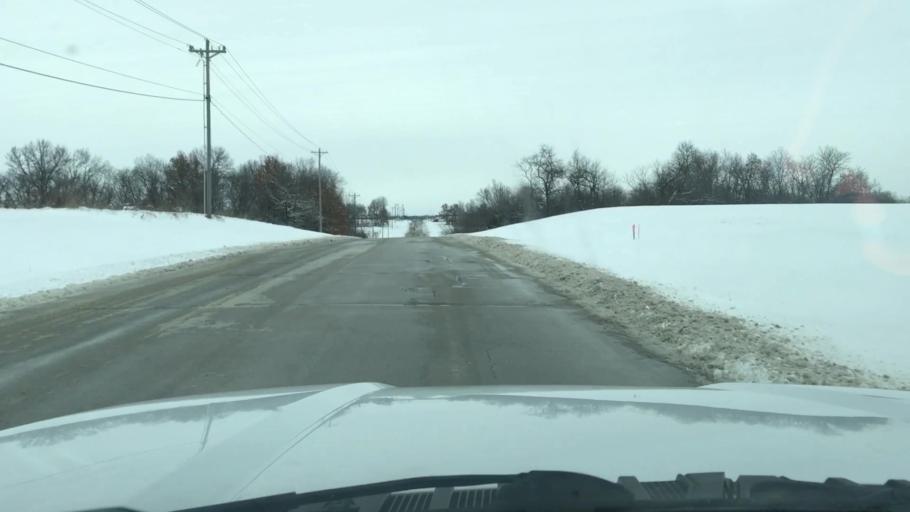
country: US
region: Missouri
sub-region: Clinton County
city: Cameron
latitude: 39.7447
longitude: -94.2153
